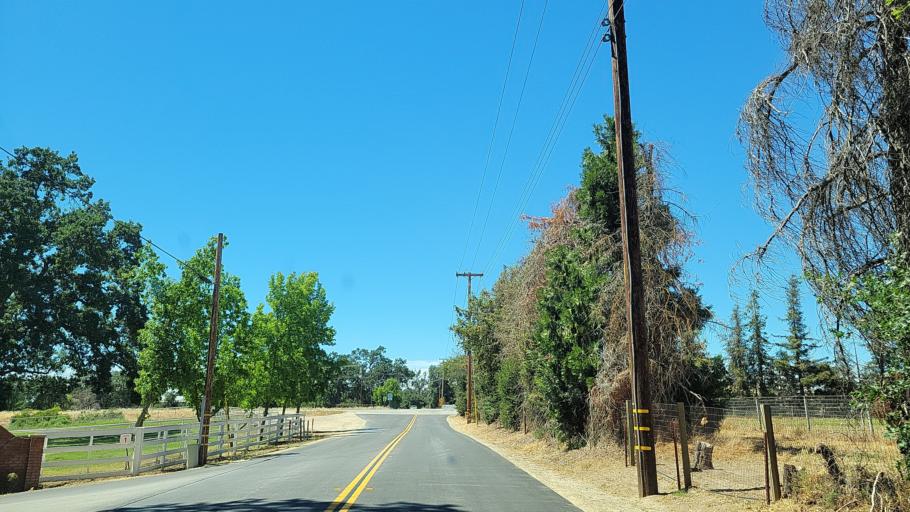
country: US
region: California
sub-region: San Luis Obispo County
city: Atascadero
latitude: 35.5035
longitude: -120.6515
